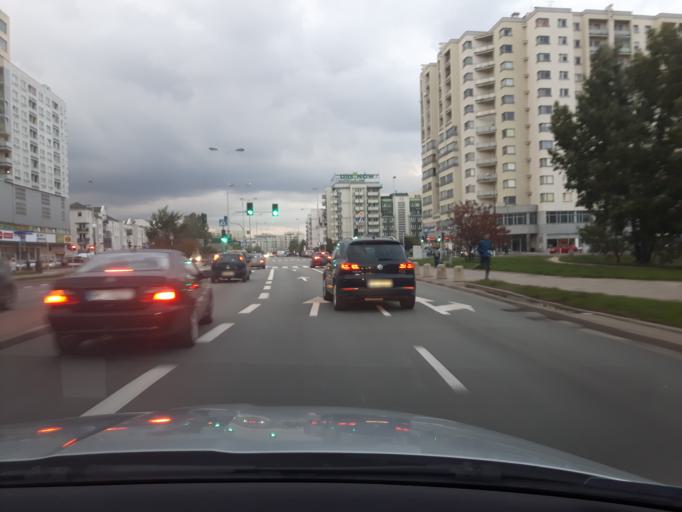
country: PL
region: Masovian Voivodeship
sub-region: Warszawa
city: Ursynow
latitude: 52.1558
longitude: 21.0354
